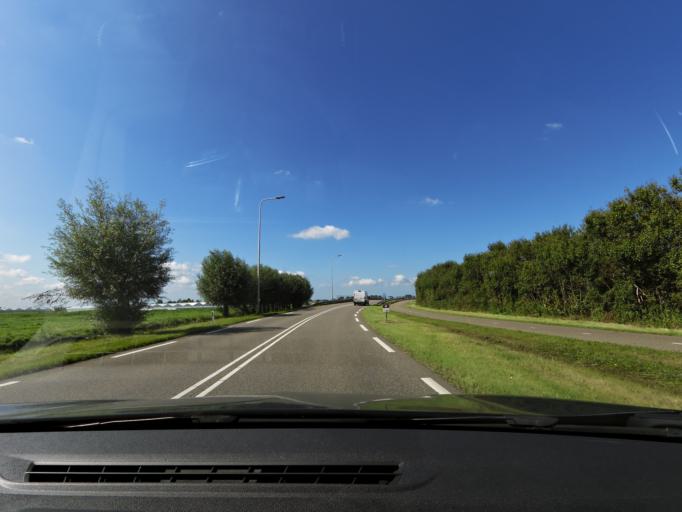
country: NL
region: North Holland
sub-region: Gemeente Aalsmeer
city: Aalsmeer
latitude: 52.2313
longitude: 4.7744
